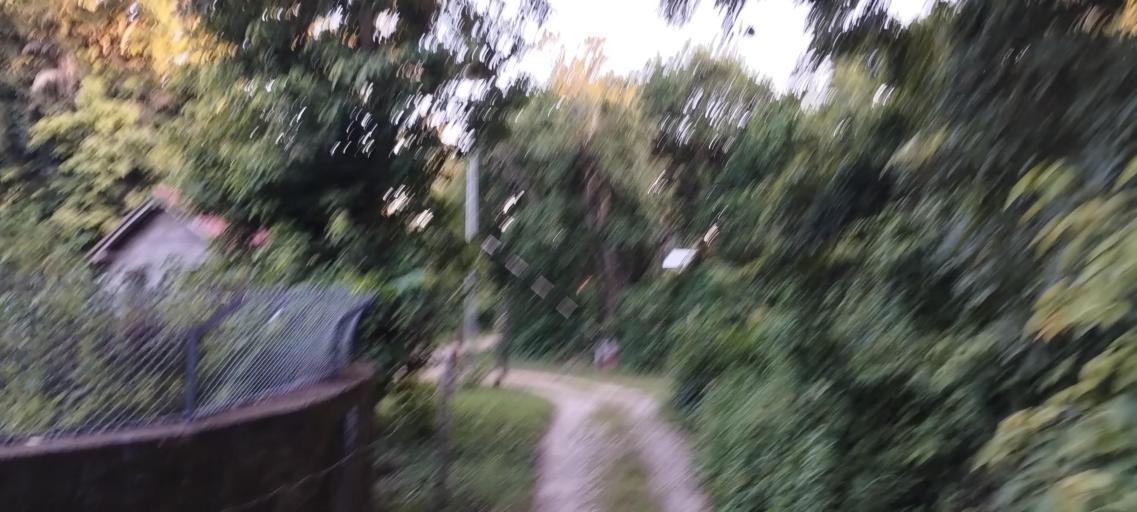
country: NP
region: Far Western
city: Tikapur
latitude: 28.4536
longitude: 81.2413
